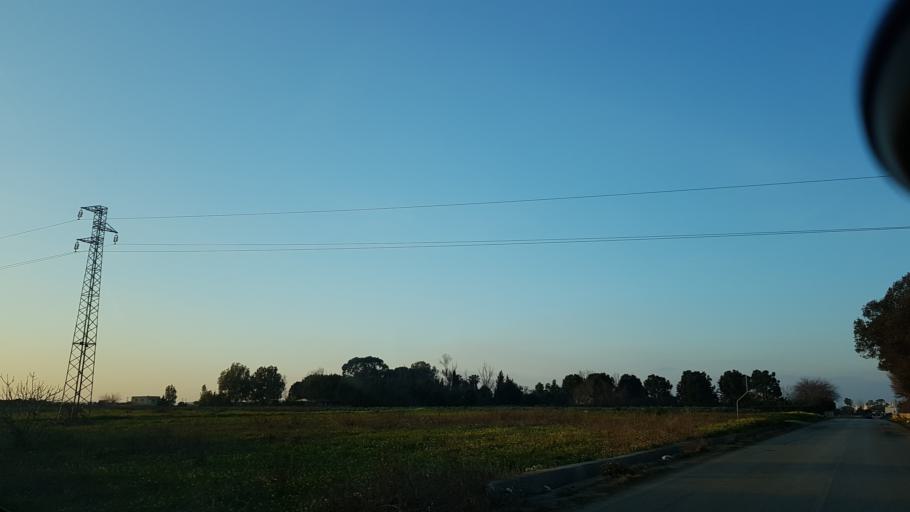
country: IT
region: Apulia
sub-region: Provincia di Brindisi
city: La Rosa
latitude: 40.6021
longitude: 17.9462
